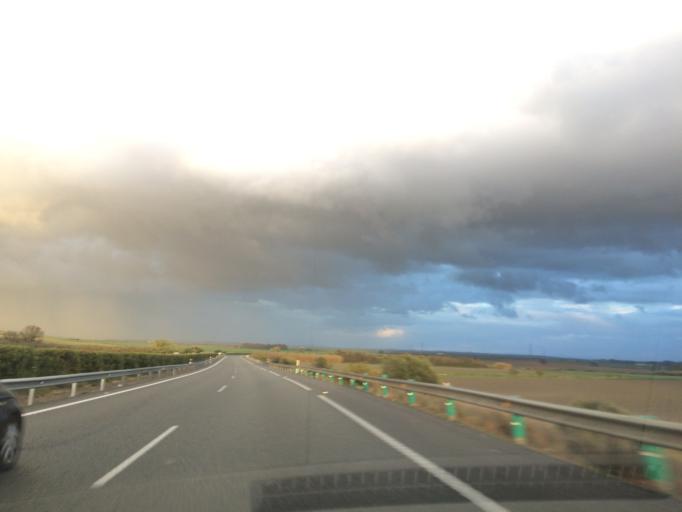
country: ES
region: Andalusia
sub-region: Provincia de Sevilla
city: Alcala de Guadaira
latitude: 37.3248
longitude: -5.7909
